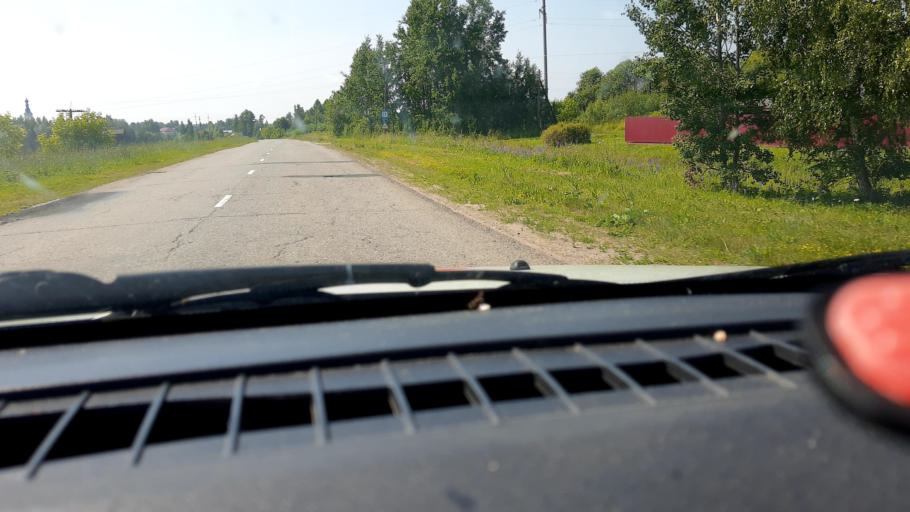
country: RU
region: Nizjnij Novgorod
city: Sharanga
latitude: 57.0575
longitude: 46.5461
